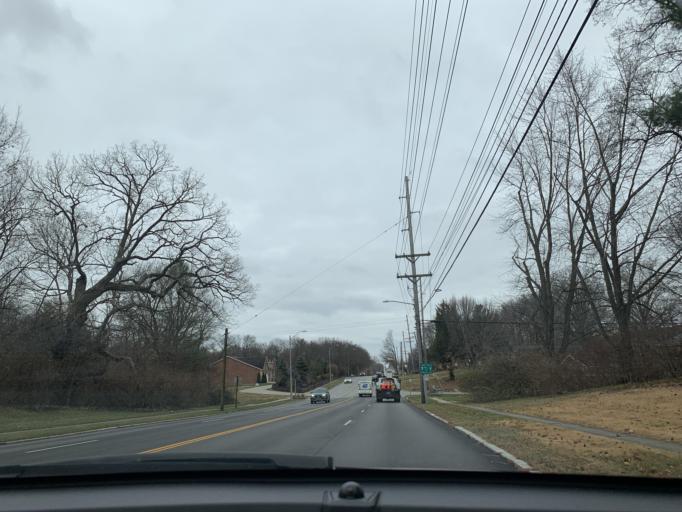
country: US
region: Illinois
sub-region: Sangamon County
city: Leland Grove
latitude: 39.7755
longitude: -89.6870
